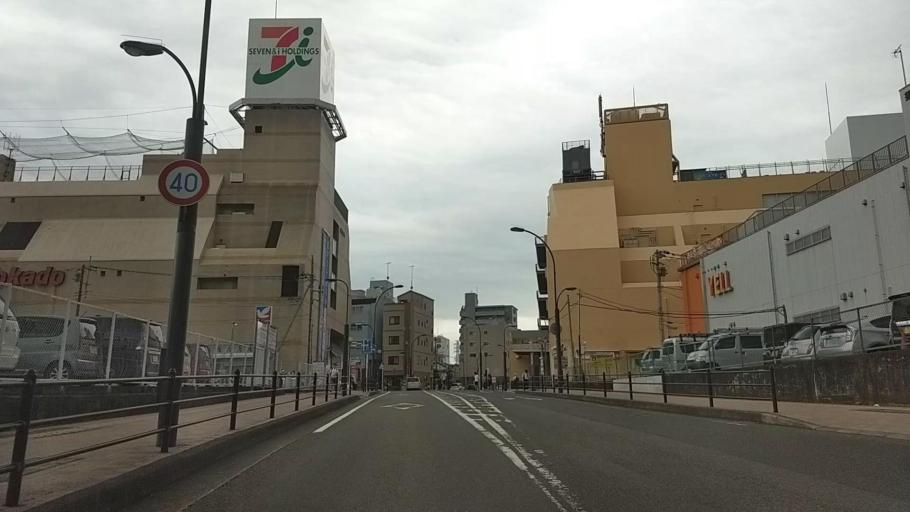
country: JP
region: Kanagawa
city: Isehara
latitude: 35.3960
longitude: 139.3150
